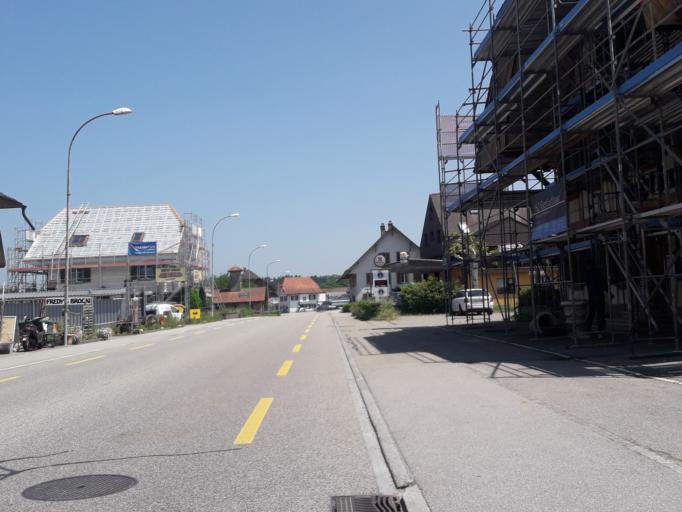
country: CH
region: Bern
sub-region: Oberaargau
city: Aarwangen
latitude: 47.2163
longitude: 7.7494
